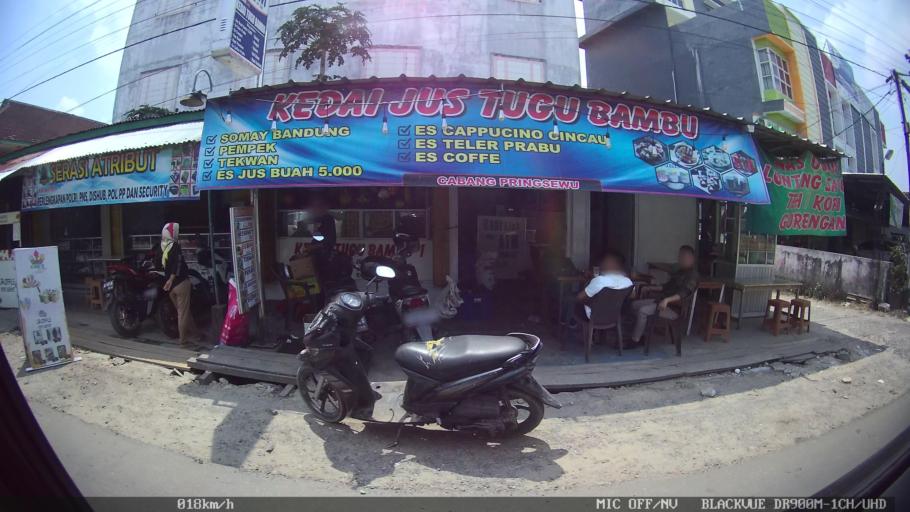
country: ID
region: Lampung
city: Pringsewu
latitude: -5.3543
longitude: 104.9730
